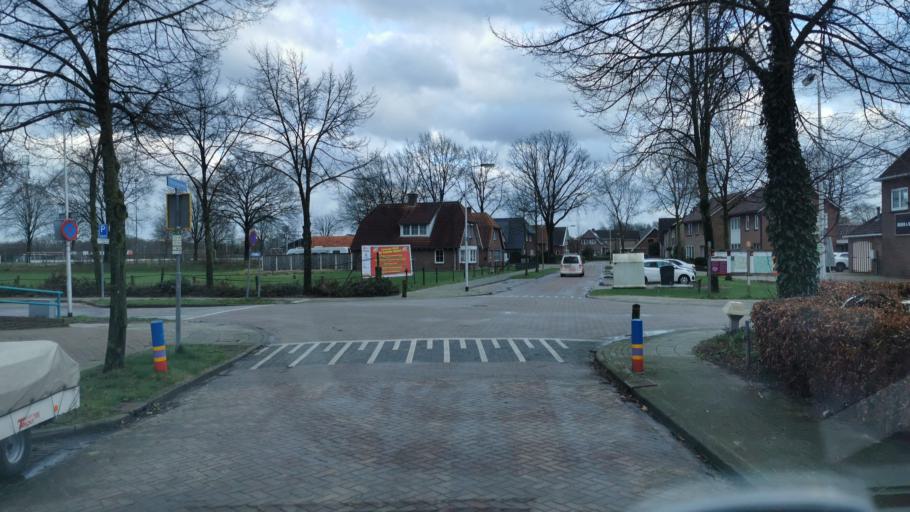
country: DE
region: Lower Saxony
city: Lage
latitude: 52.4269
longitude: 6.9761
